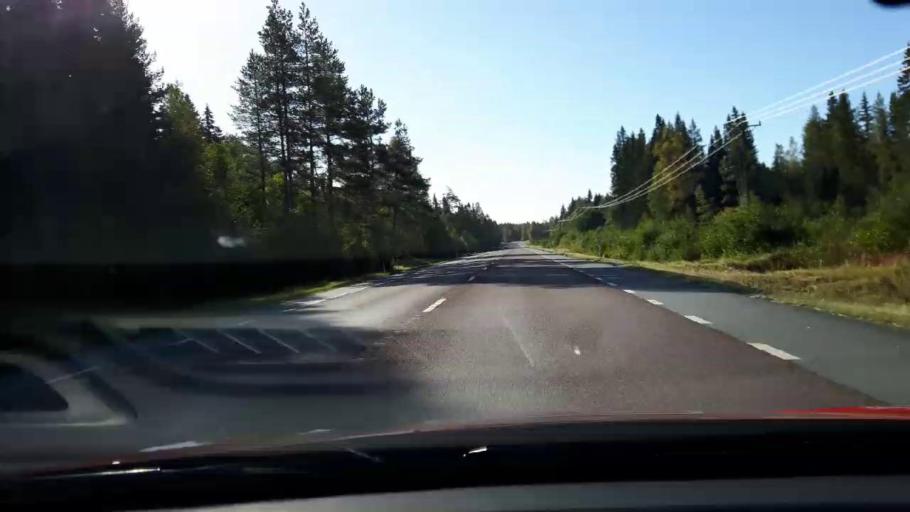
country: SE
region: Jaemtland
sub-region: Braecke Kommun
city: Braecke
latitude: 62.8578
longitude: 15.3173
